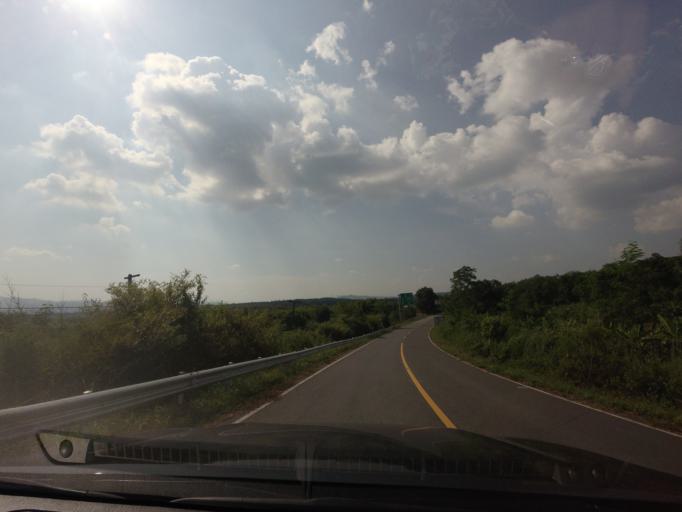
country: TH
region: Nan
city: Santi Suk
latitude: 18.9825
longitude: 100.9423
